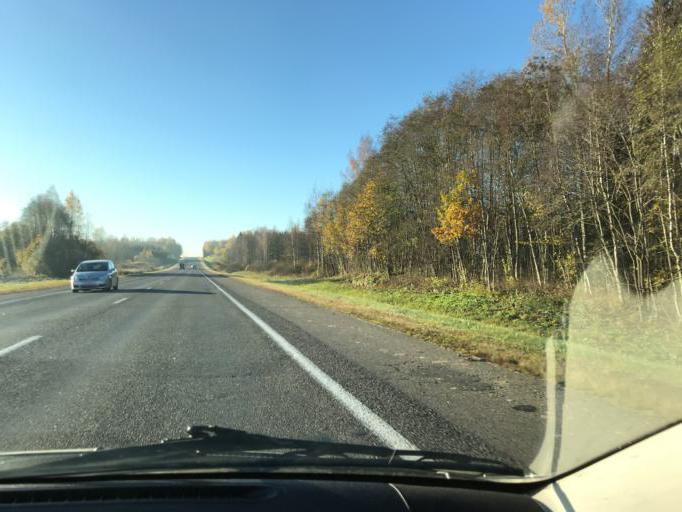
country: BY
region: Vitebsk
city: Vitebsk
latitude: 54.9204
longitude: 30.3747
